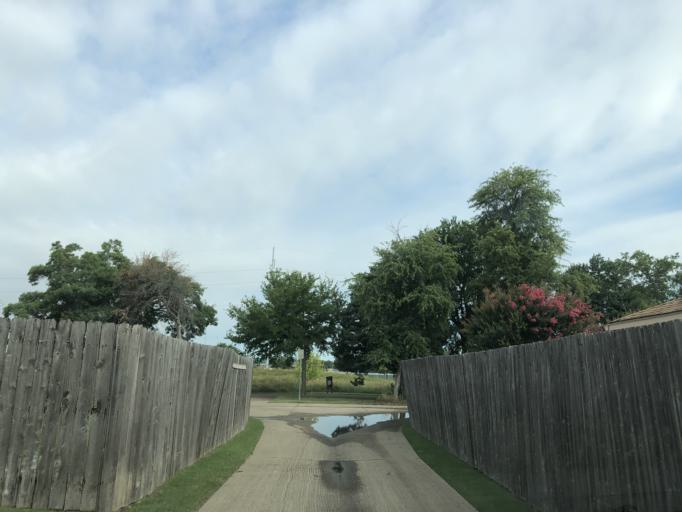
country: US
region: Texas
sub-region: Dallas County
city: Sunnyvale
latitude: 32.8437
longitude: -96.6149
